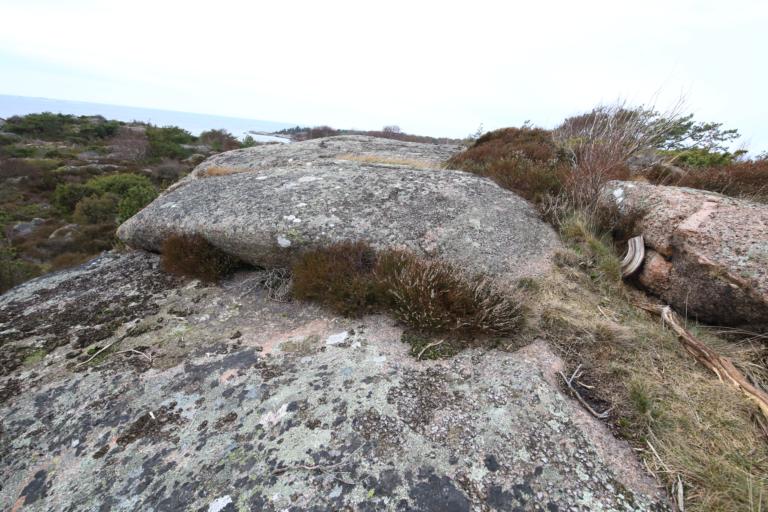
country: SE
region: Halland
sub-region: Varbergs Kommun
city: Varberg
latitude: 57.1872
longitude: 12.1758
